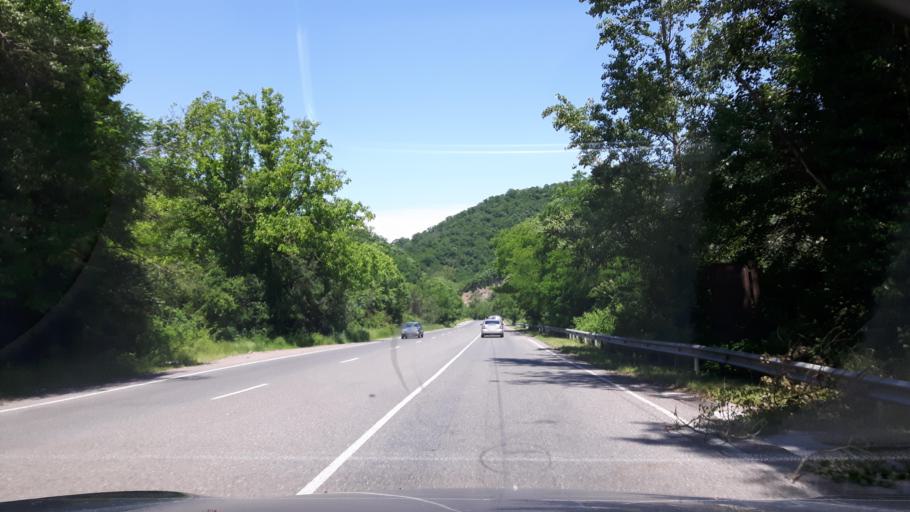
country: GE
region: Kakheti
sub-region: Gurjaani
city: Gurjaani
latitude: 41.6655
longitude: 45.8333
